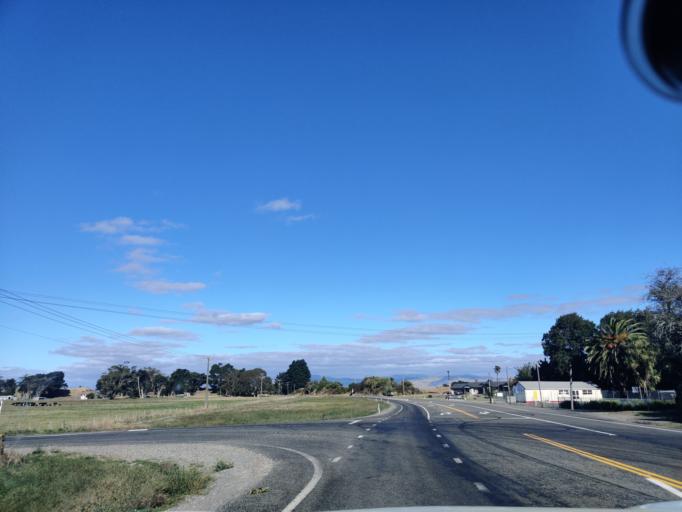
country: NZ
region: Manawatu-Wanganui
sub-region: Horowhenua District
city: Foxton
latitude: -40.4079
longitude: 175.3768
